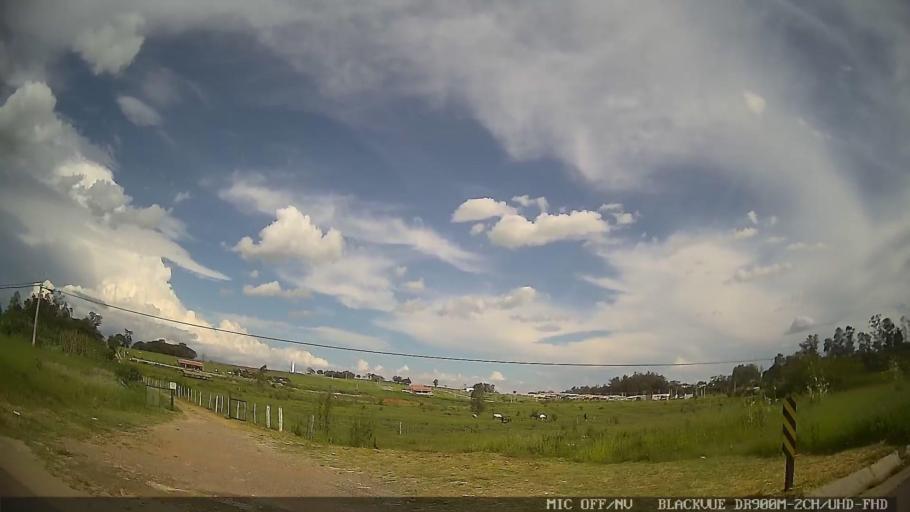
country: BR
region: Sao Paulo
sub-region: Conchas
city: Conchas
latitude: -23.0626
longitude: -47.9693
